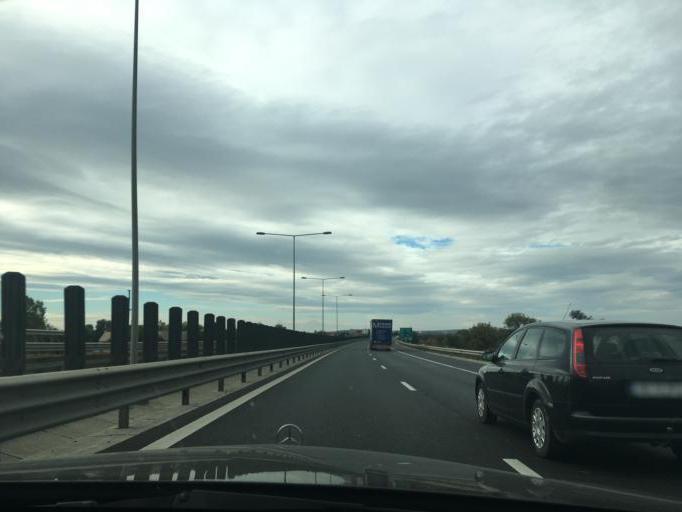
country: RO
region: Sibiu
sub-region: Municipiul Sibiu
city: Sibiu
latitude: 45.8037
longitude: 24.1817
